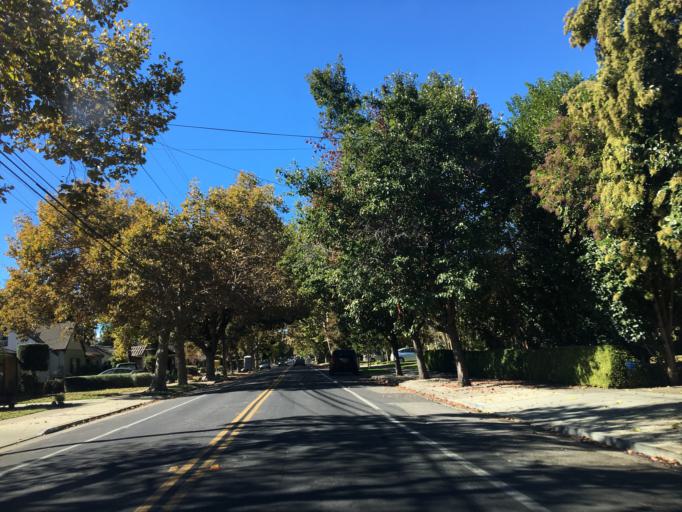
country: US
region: California
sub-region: Santa Clara County
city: Buena Vista
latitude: 37.2978
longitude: -121.8951
